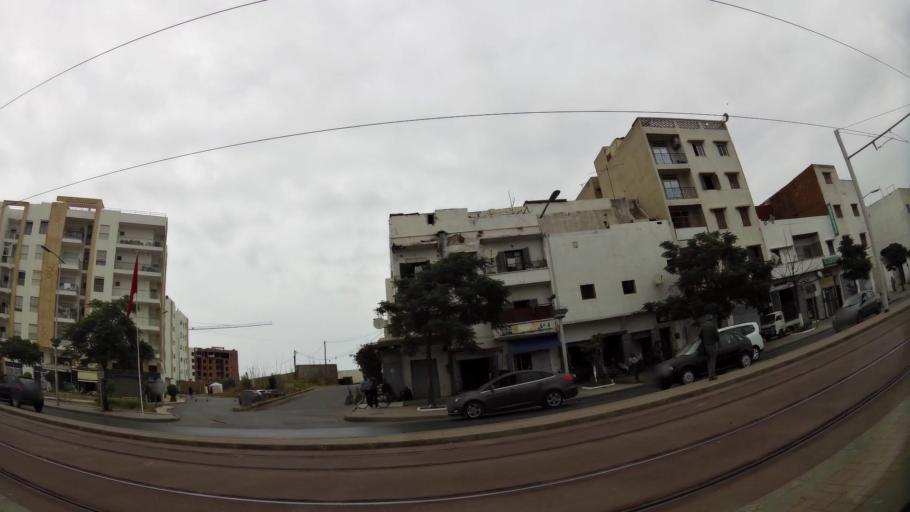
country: MA
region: Rabat-Sale-Zemmour-Zaer
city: Sale
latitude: 34.0350
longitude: -6.8089
